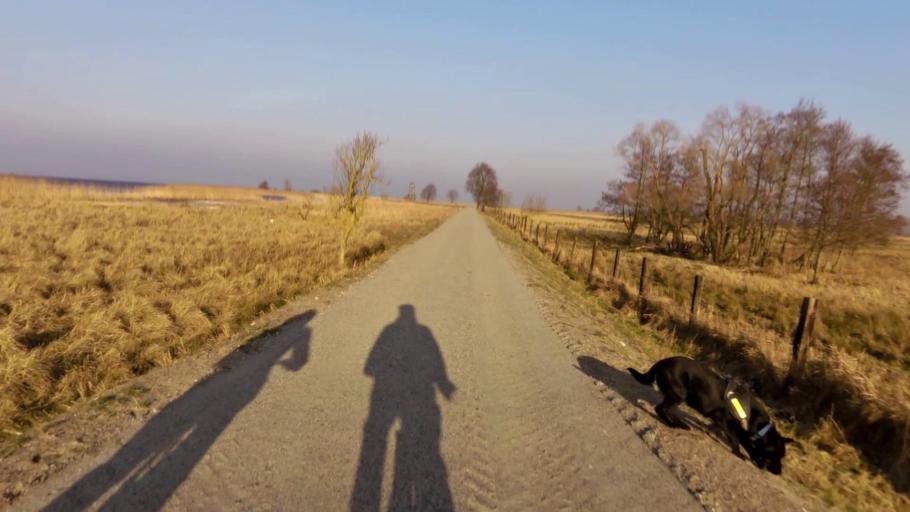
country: PL
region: West Pomeranian Voivodeship
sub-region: Powiat kamienski
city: Wolin
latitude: 53.7507
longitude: 14.5593
